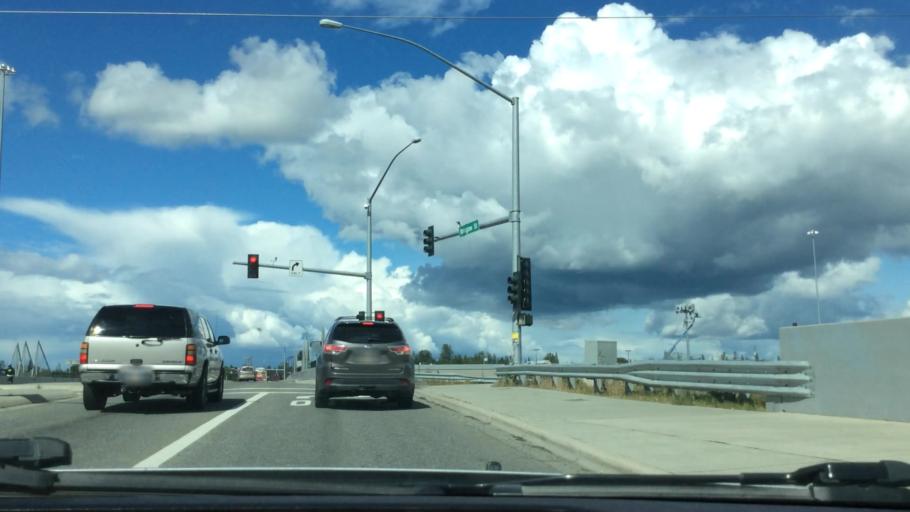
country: US
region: Alaska
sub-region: Anchorage Municipality
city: Anchorage
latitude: 61.2204
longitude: -149.8082
